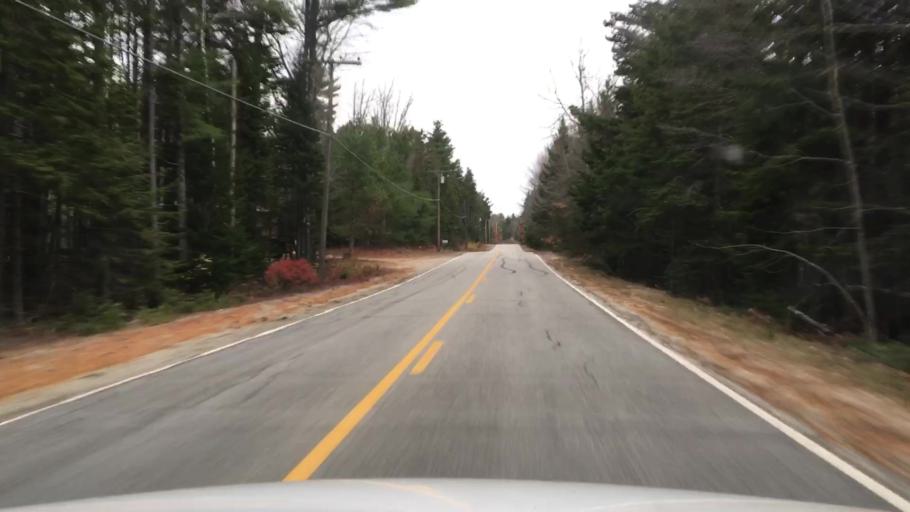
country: US
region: Maine
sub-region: Hancock County
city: Sedgwick
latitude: 44.2837
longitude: -68.5545
